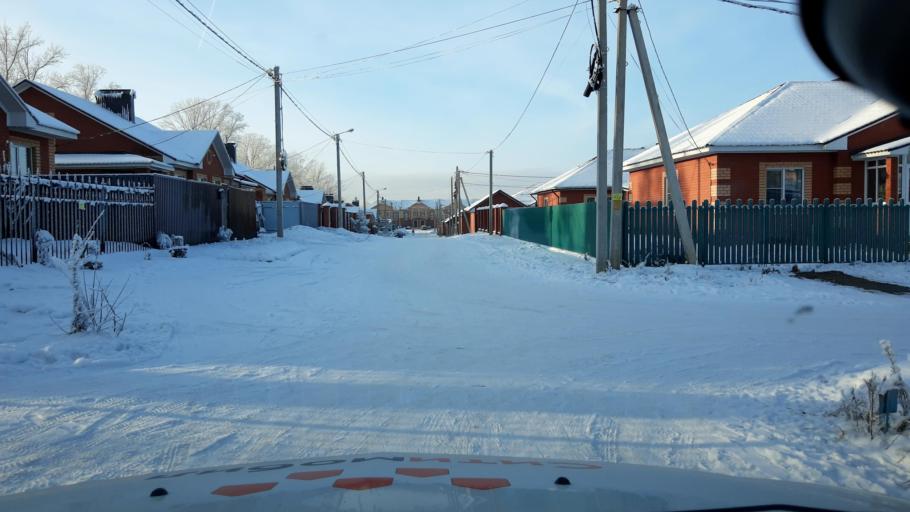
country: RU
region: Bashkortostan
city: Mikhaylovka
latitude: 54.8290
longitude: 55.8722
